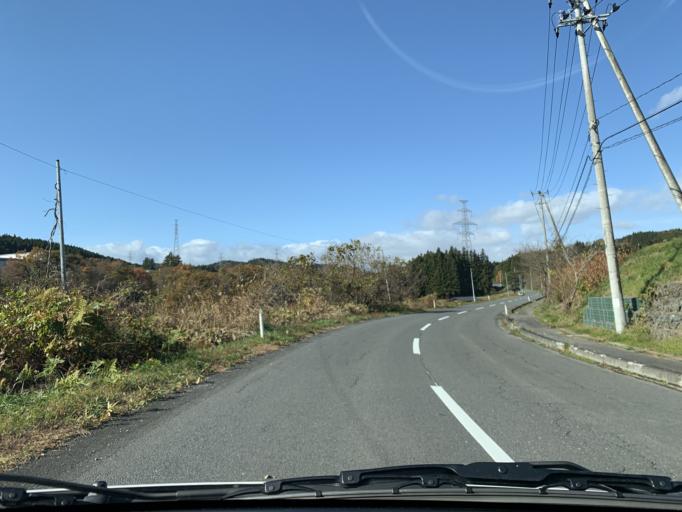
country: JP
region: Iwate
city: Ichinoseki
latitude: 39.0238
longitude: 141.1120
